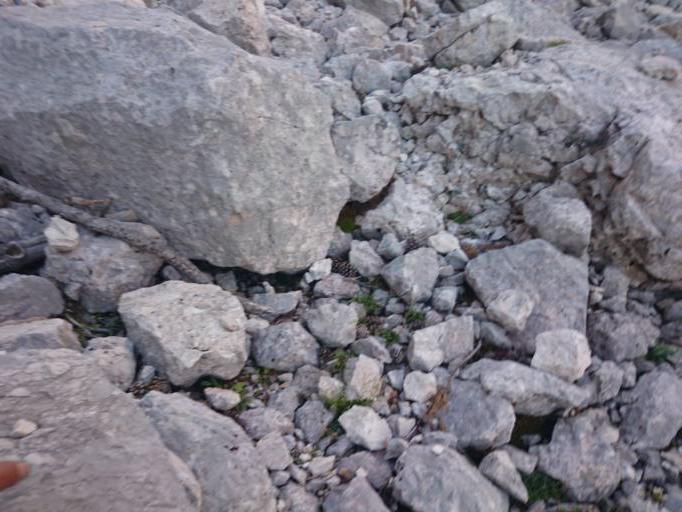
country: AL
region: Elbasan
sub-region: Rrethi i Gramshit
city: Kushove
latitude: 40.7188
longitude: 20.1456
